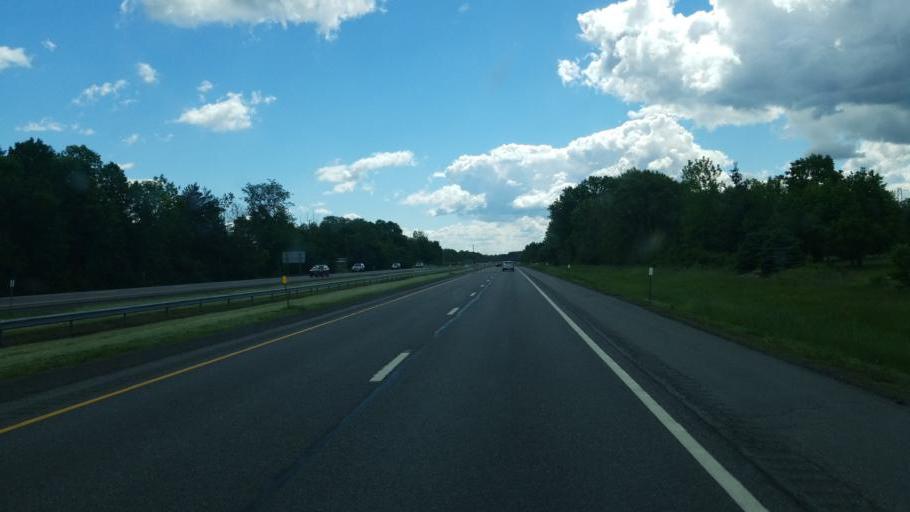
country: US
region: New York
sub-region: Madison County
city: Canastota
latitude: 43.0921
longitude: -75.7853
